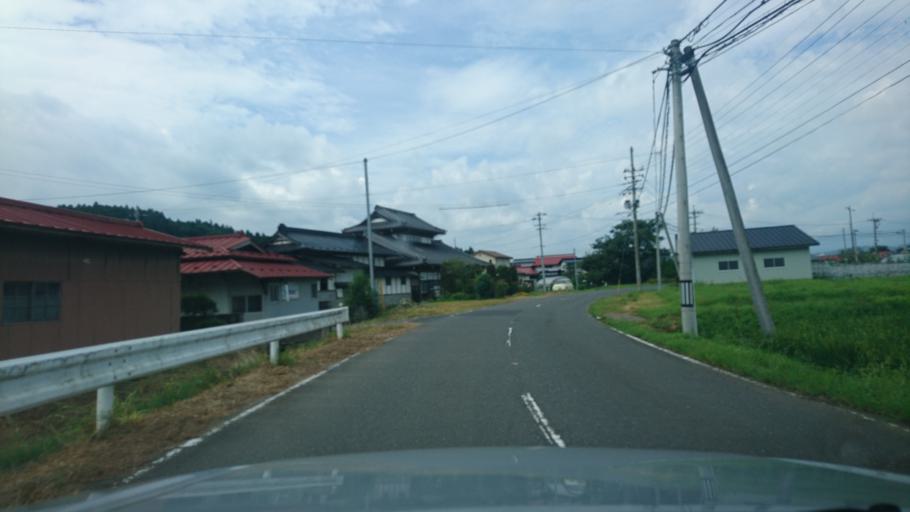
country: JP
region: Iwate
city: Ichinoseki
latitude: 38.7942
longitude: 140.9950
